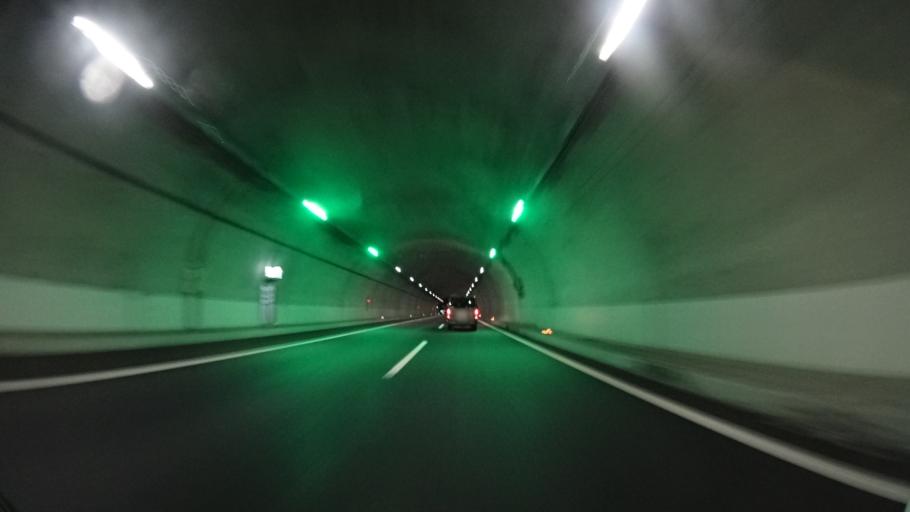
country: JP
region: Osaka
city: Takatsuki
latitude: 34.8960
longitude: 135.6070
